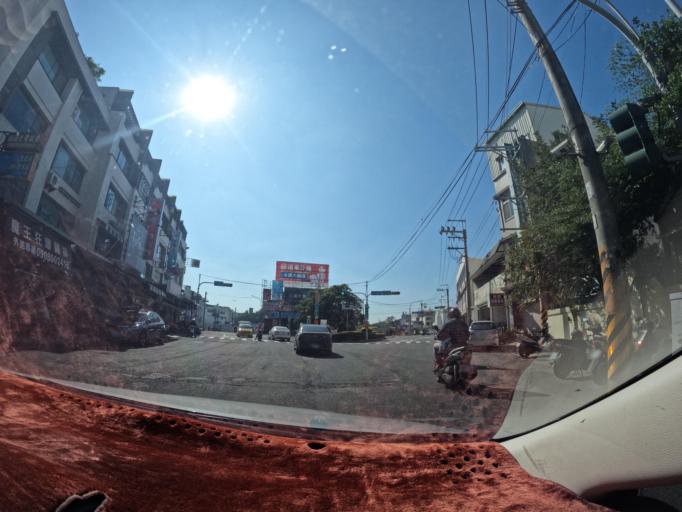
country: TW
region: Taiwan
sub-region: Tainan
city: Tainan
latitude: 23.0174
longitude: 120.2435
